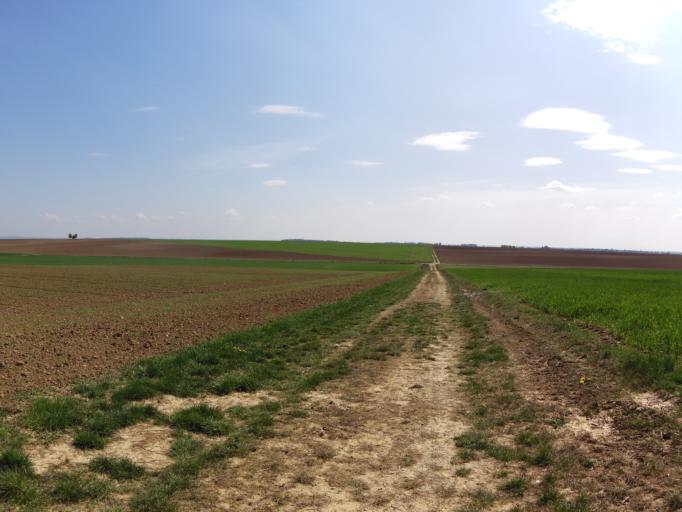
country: DE
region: Bavaria
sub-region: Regierungsbezirk Unterfranken
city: Giebelstadt
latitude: 49.6881
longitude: 9.9538
